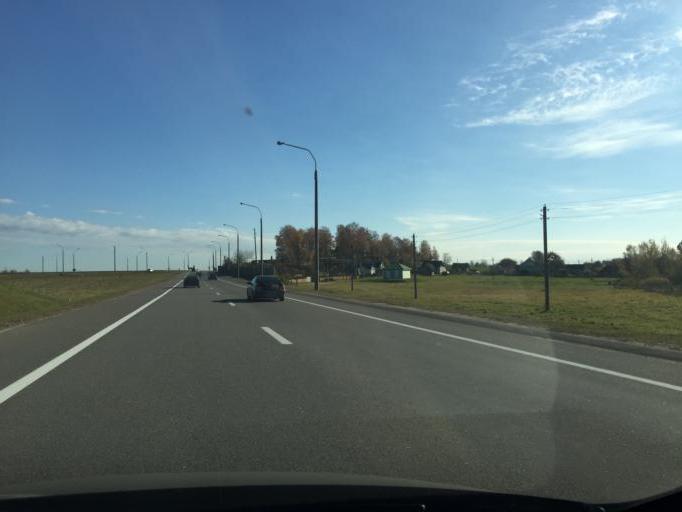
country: BY
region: Minsk
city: Slabada
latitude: 54.0139
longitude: 27.8888
